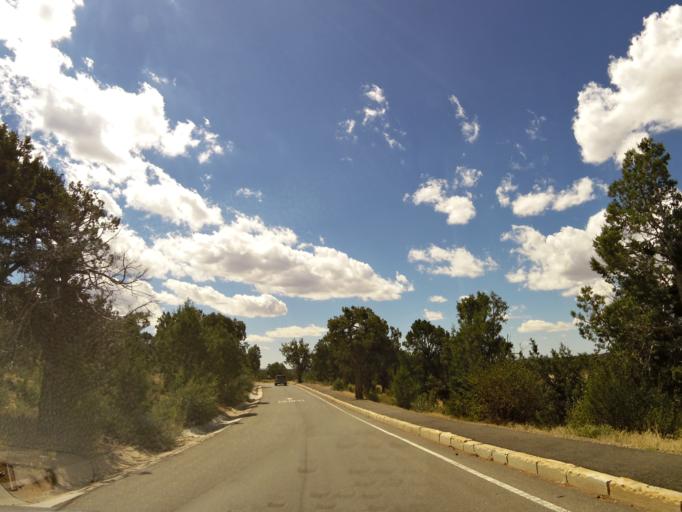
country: US
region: Colorado
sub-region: Montezuma County
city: Cortez
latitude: 37.1849
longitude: -108.4903
